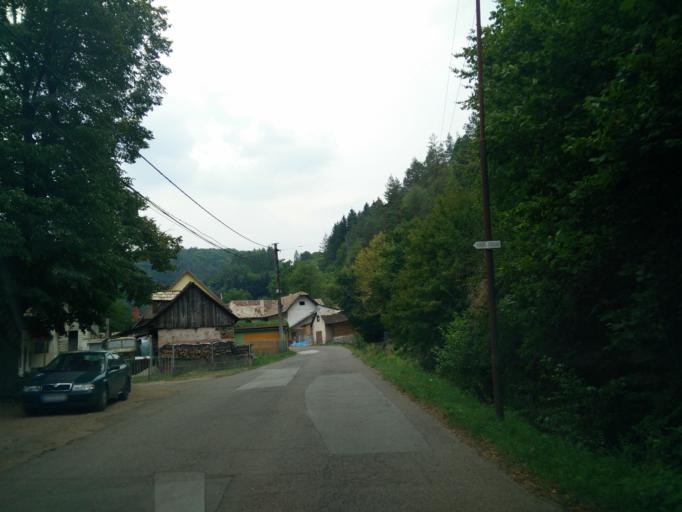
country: SK
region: Banskobystricky
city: Ziar nad Hronom
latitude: 48.5790
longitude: 18.8970
